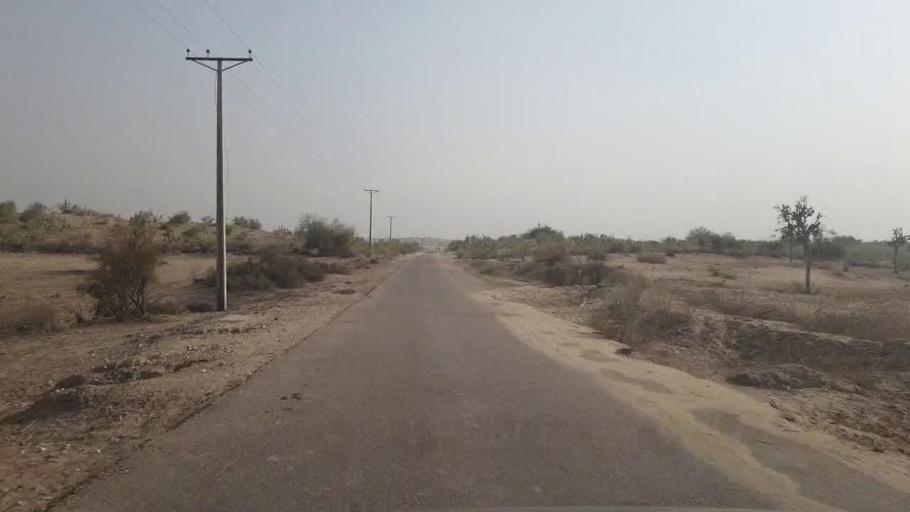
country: PK
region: Sindh
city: Chor
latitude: 25.5439
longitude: 69.9597
